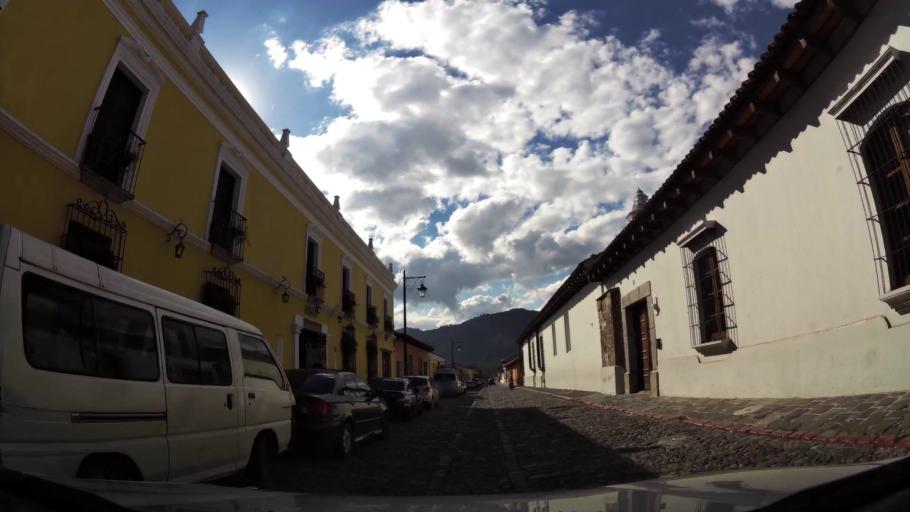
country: GT
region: Sacatepequez
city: Antigua Guatemala
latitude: 14.5583
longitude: -90.7326
